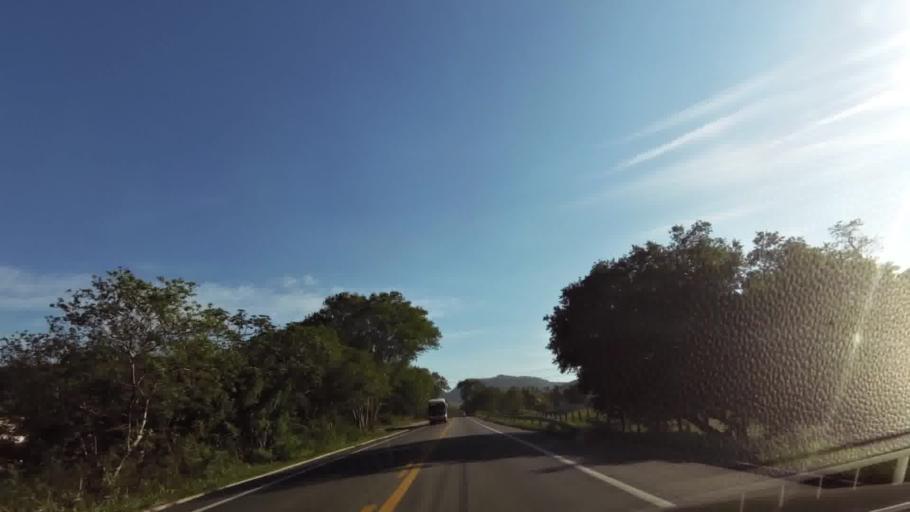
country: BR
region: Espirito Santo
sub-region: Viana
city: Viana
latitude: -20.4134
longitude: -40.4595
